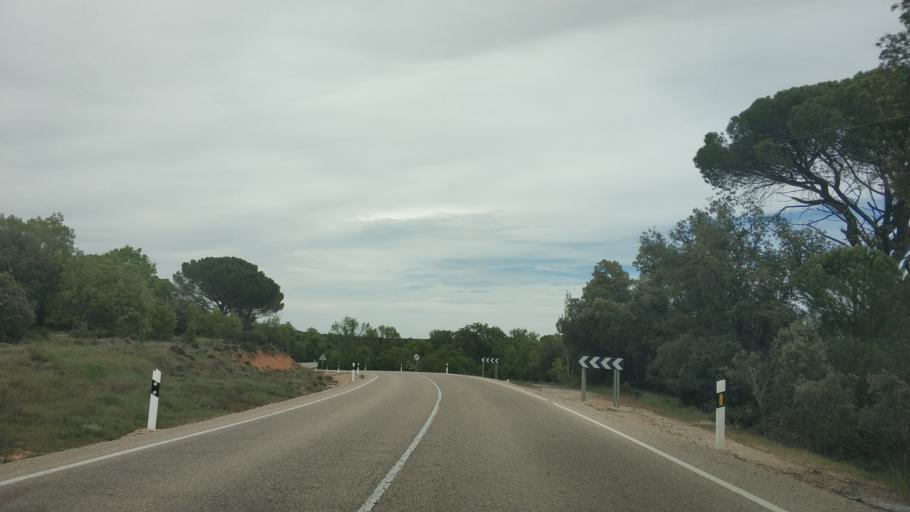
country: ES
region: Castille and Leon
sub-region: Provincia de Soria
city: Bayubas de Abajo
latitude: 41.5045
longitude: -2.8973
